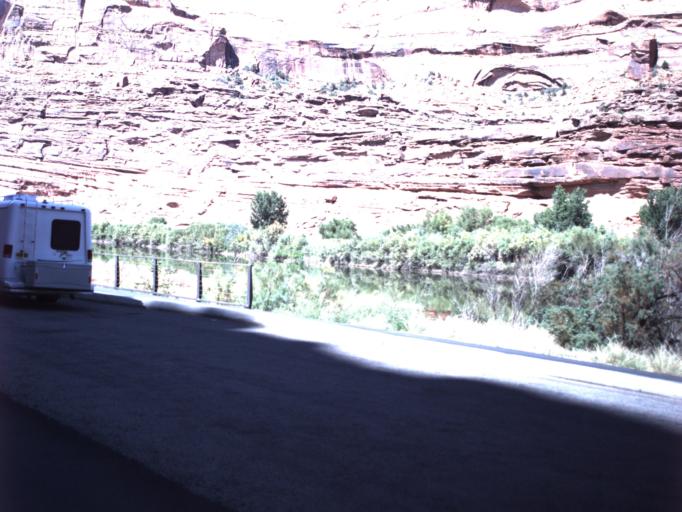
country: US
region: Utah
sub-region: Grand County
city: Moab
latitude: 38.6018
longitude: -109.5671
